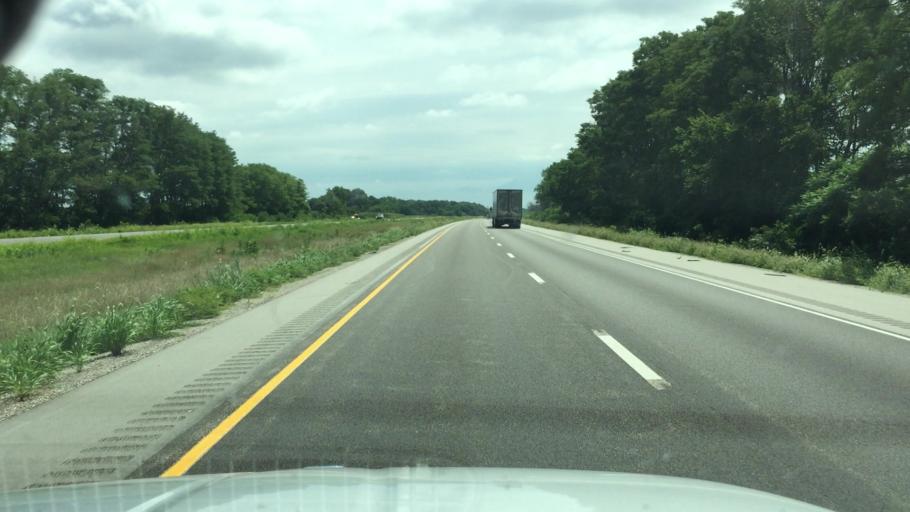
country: US
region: Illinois
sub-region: Peoria County
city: Elmwood
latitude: 40.8662
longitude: -90.0275
